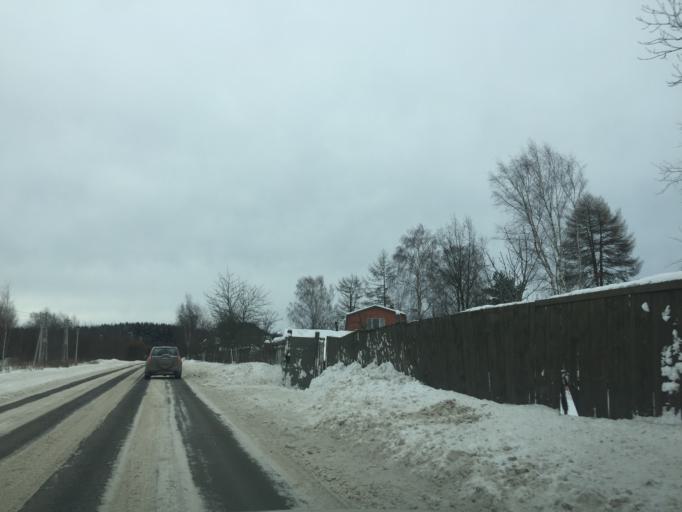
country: RU
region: Leningrad
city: Imeni Sverdlova
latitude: 59.7873
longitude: 30.7137
